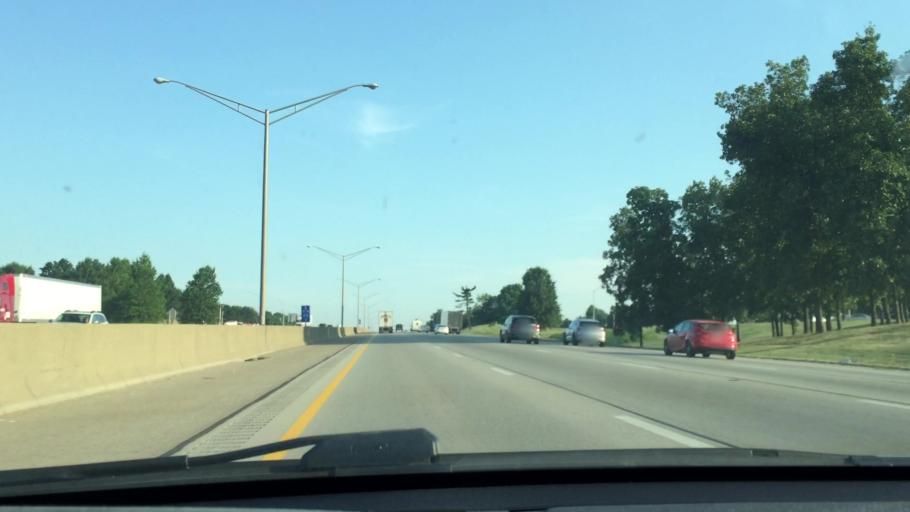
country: US
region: Kentucky
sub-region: Boone County
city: Union
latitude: 38.9403
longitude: -84.6324
